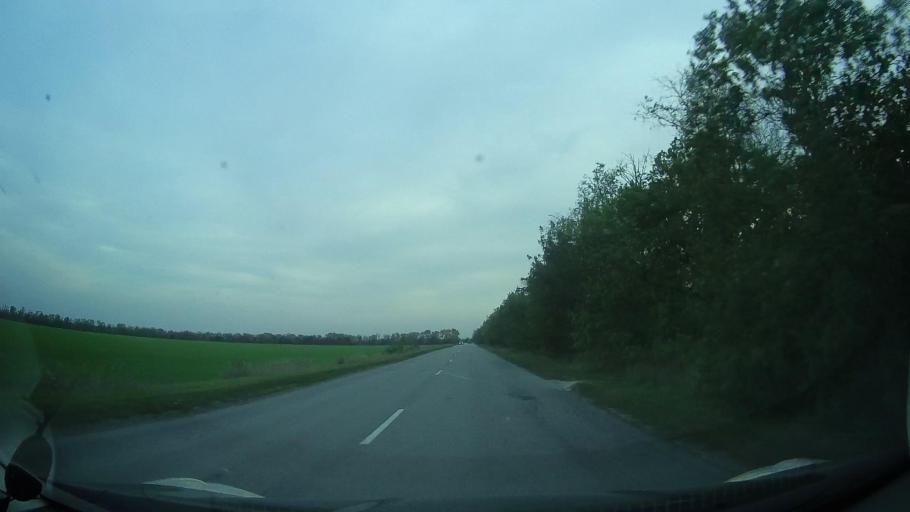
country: RU
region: Rostov
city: Kirovskaya
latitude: 47.0063
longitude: 39.9789
